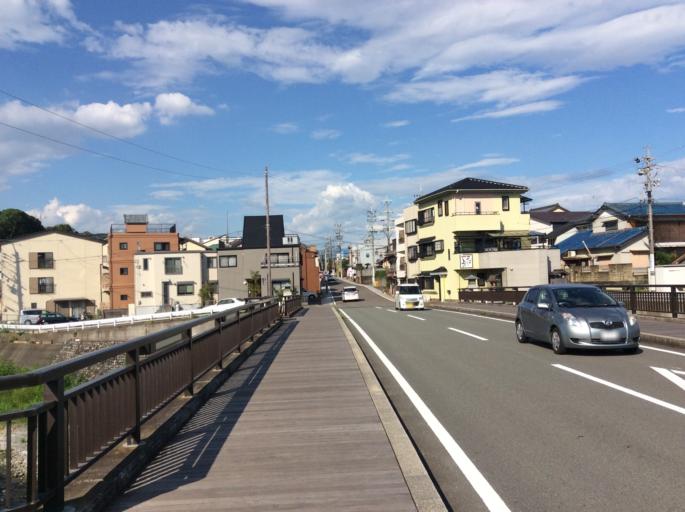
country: JP
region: Shizuoka
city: Fujinomiya
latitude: 35.1062
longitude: 138.5649
